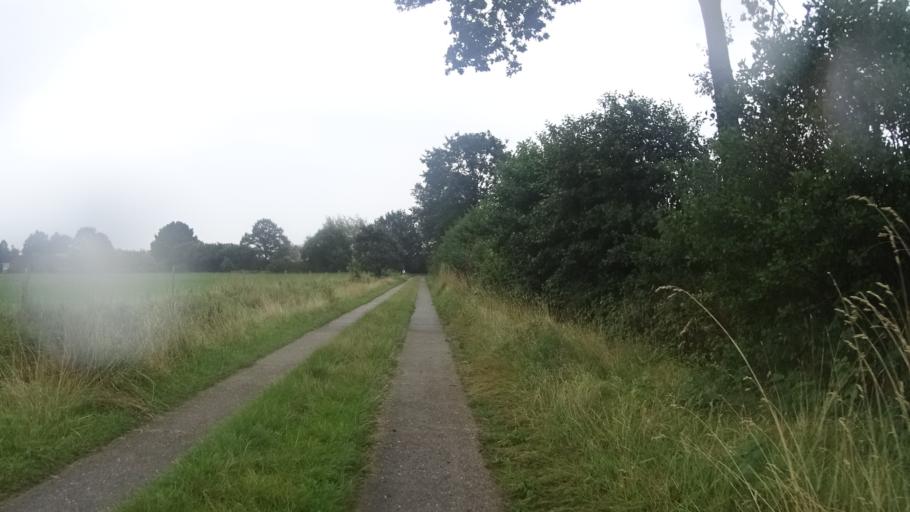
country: DE
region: Schleswig-Holstein
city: Hemdingen
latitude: 53.7602
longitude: 9.8155
